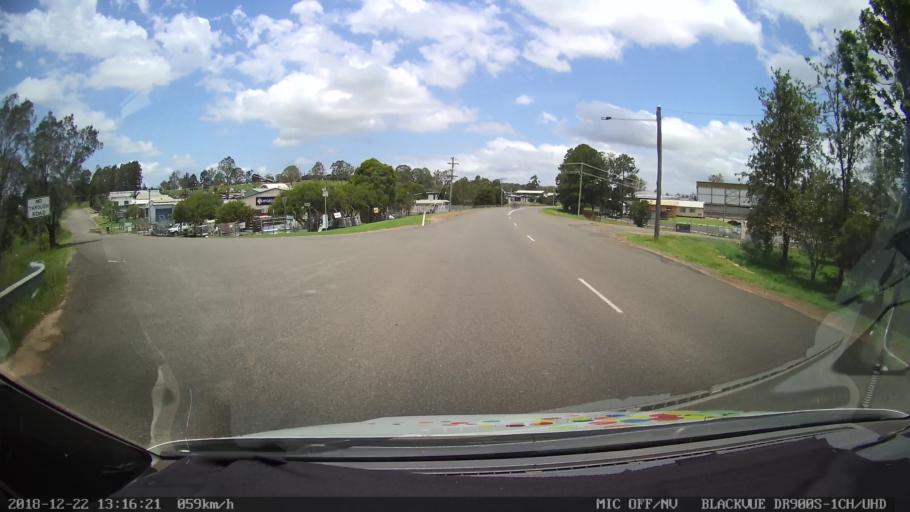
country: AU
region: New South Wales
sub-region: Clarence Valley
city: South Grafton
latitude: -29.7253
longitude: 152.9392
